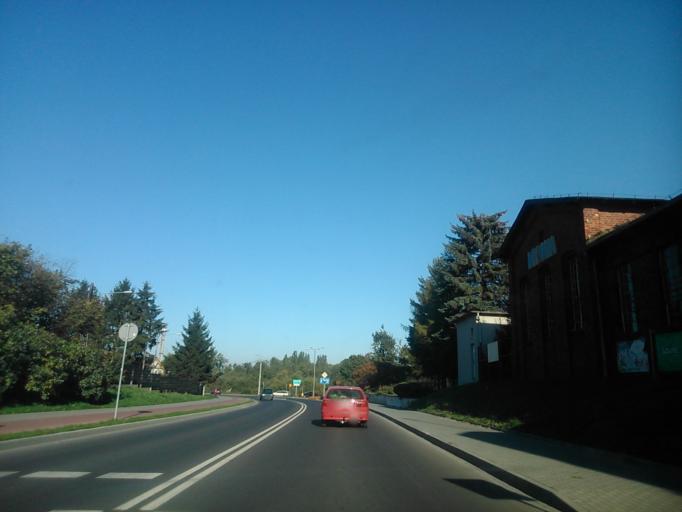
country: PL
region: Kujawsko-Pomorskie
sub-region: Powiat wabrzeski
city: Wabrzezno
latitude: 53.2774
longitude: 18.9644
